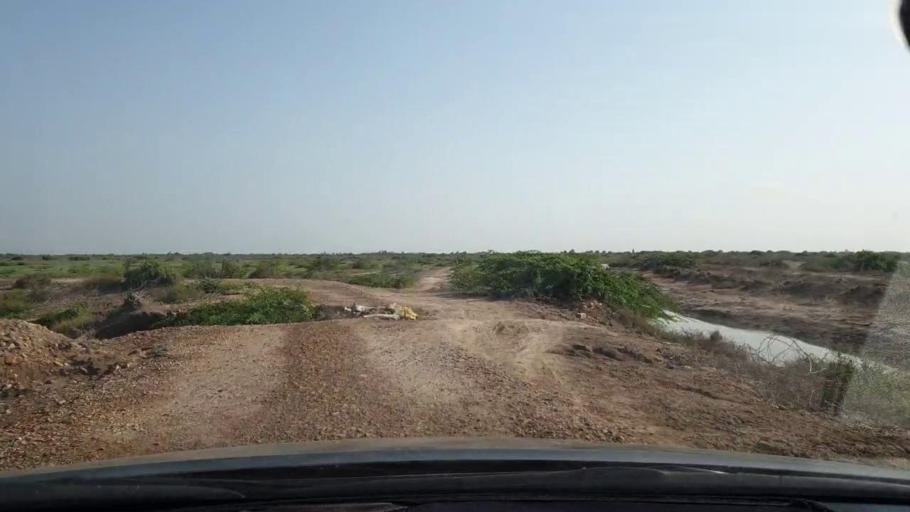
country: PK
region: Sindh
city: Naukot
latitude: 24.8341
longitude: 69.2370
